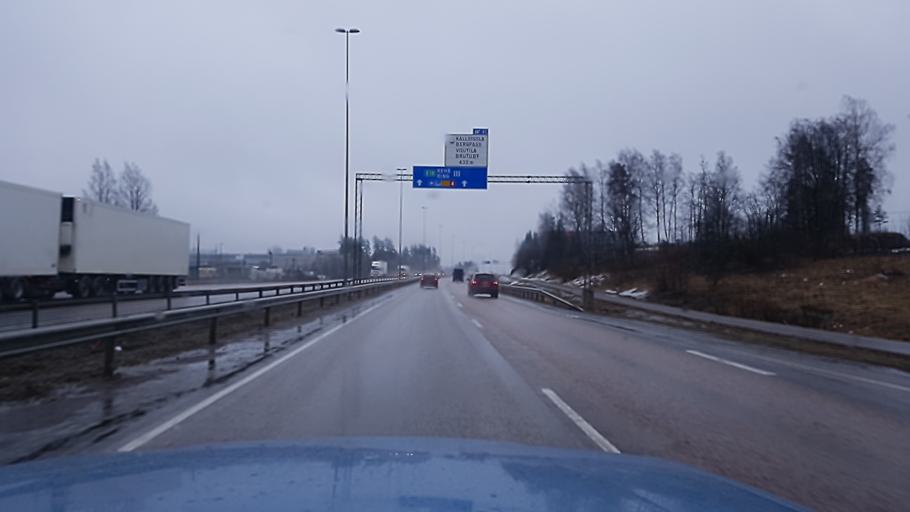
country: FI
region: Uusimaa
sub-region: Helsinki
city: Teekkarikylae
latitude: 60.2983
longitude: 24.9016
